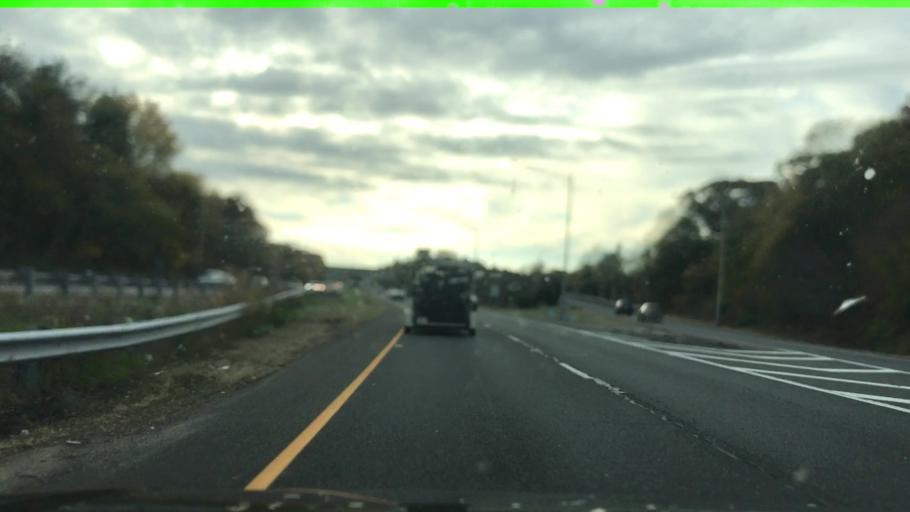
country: US
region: New Jersey
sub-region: Monmouth County
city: Eatontown
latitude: 40.2912
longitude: -74.0696
